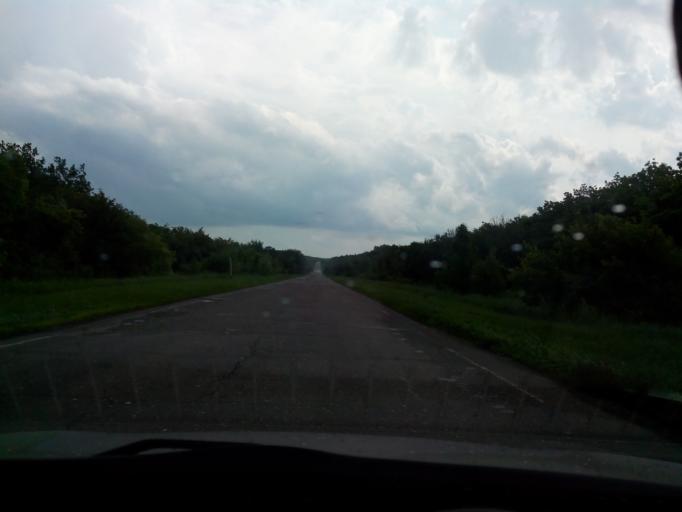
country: RU
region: Volgograd
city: Mikhaylovka
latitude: 49.9093
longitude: 42.9428
